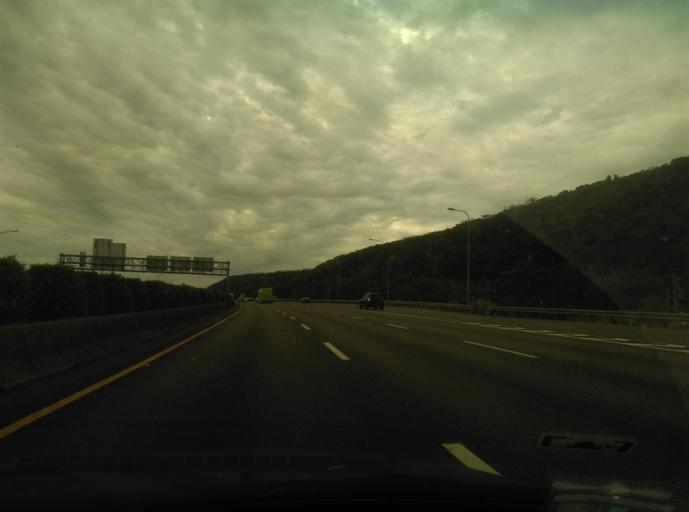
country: TW
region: Taiwan
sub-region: Taoyuan
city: Taoyuan
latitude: 24.9379
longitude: 121.3206
